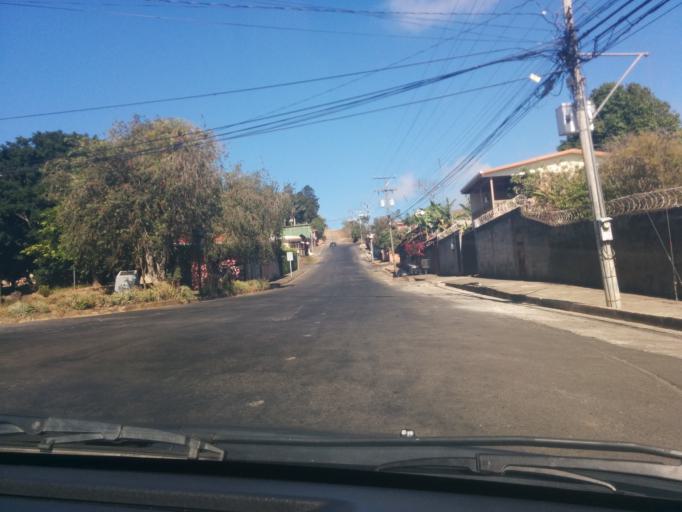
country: CR
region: Alajuela
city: San Ramon
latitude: 10.0827
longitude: -84.4739
